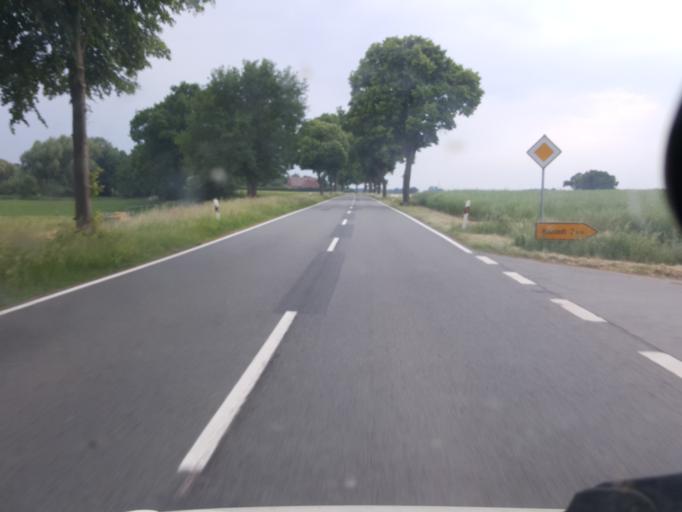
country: DE
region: Lower Saxony
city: Raddestorf
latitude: 52.4807
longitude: 8.9952
